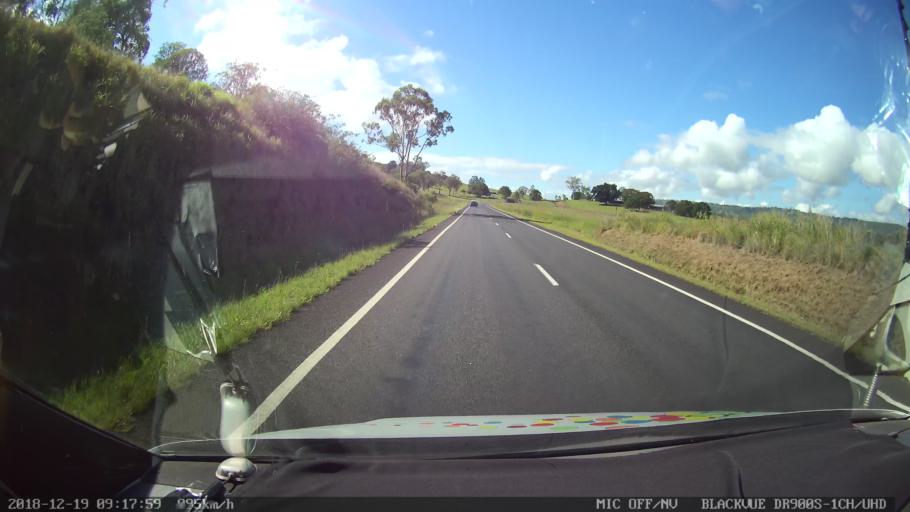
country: AU
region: New South Wales
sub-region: Kyogle
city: Kyogle
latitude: -28.5413
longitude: 152.9759
